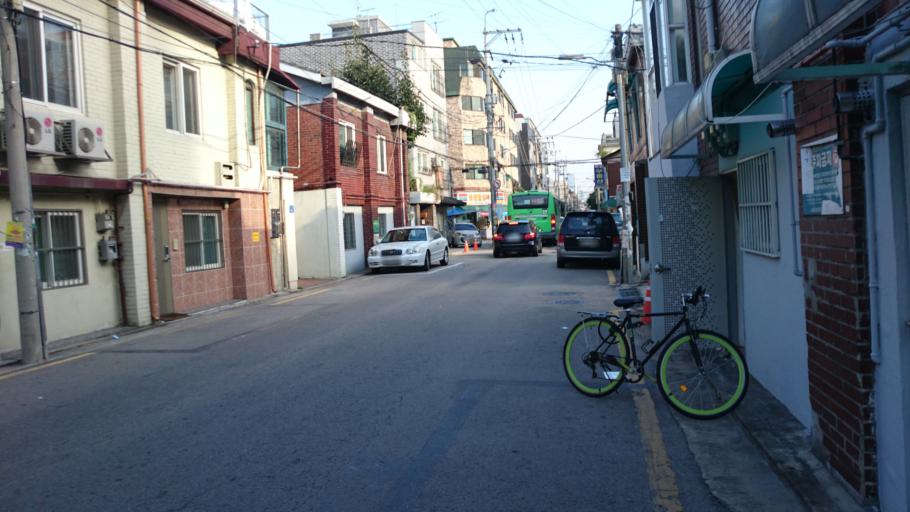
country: KR
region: Seoul
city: Seoul
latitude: 37.5607
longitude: 126.8991
